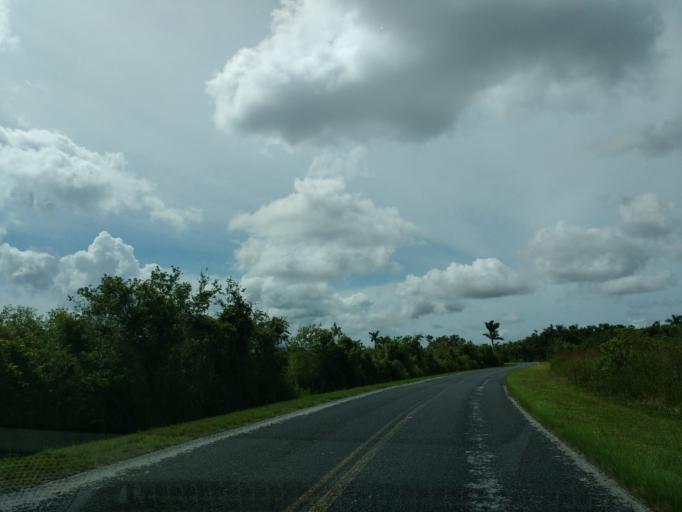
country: US
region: Florida
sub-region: Miami-Dade County
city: Florida City
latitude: 25.3864
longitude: -80.6113
